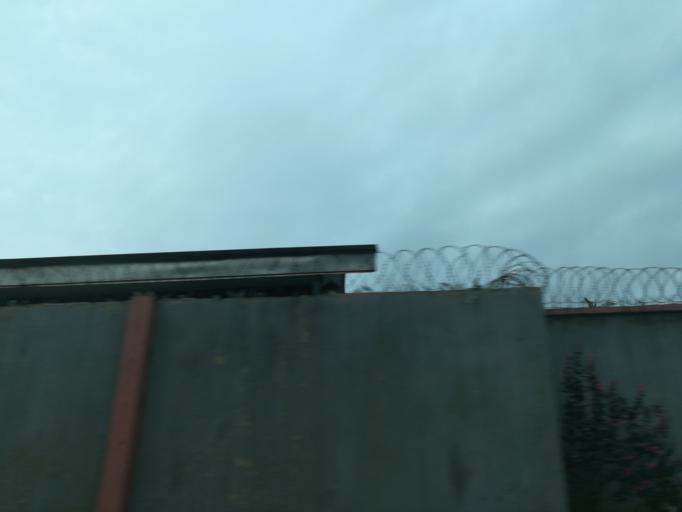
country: NG
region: Rivers
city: Port Harcourt
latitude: 4.8174
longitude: 7.0260
